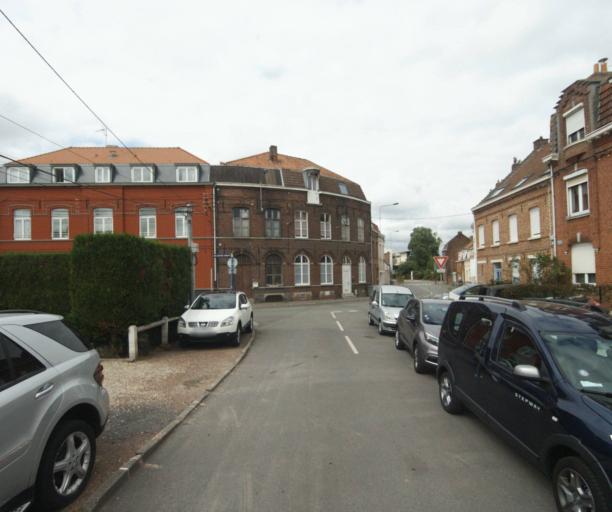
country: FR
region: Nord-Pas-de-Calais
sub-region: Departement du Nord
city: Villeneuve-d'Ascq
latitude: 50.6172
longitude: 3.1583
